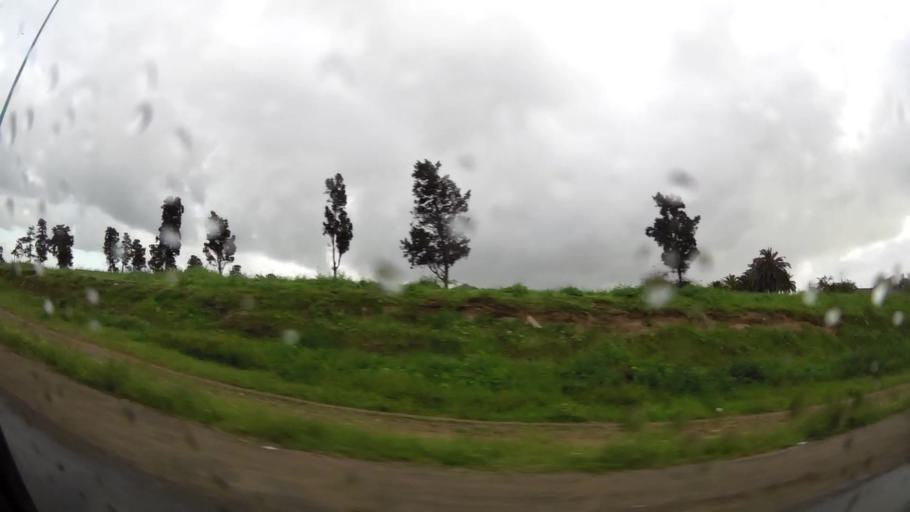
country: MA
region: Grand Casablanca
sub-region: Mohammedia
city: Mohammedia
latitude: 33.6761
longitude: -7.4095
